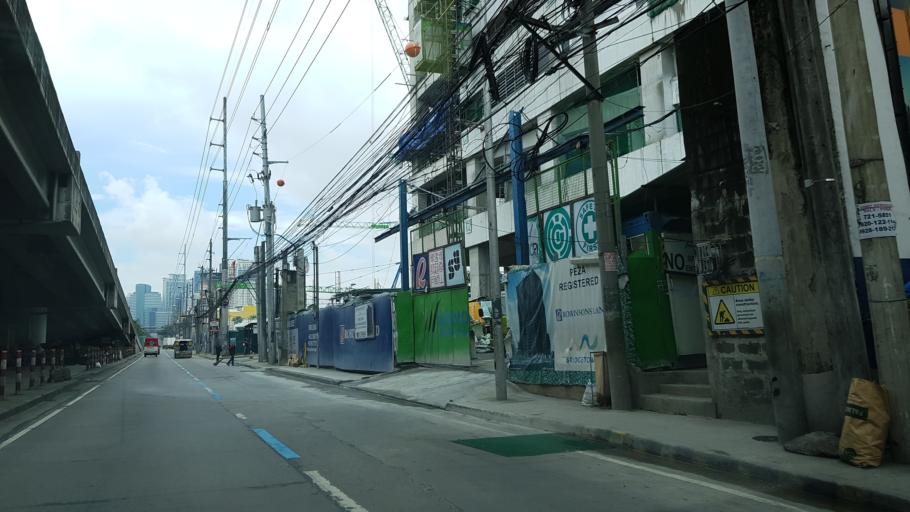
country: PH
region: Metro Manila
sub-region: Pasig
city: Pasig City
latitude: 14.5917
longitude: 121.0800
